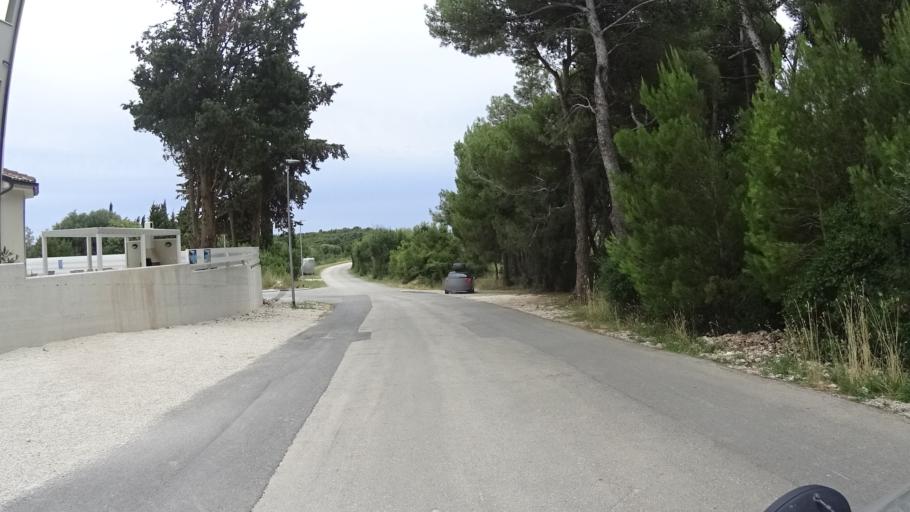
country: HR
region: Istarska
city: Medulin
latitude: 44.8020
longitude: 13.9062
